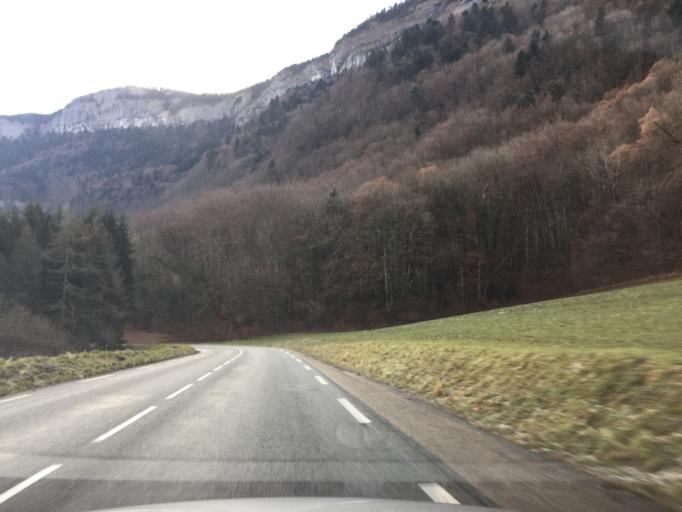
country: FR
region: Rhone-Alpes
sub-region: Departement de la Haute-Savoie
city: Gruffy
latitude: 45.7555
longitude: 6.0601
